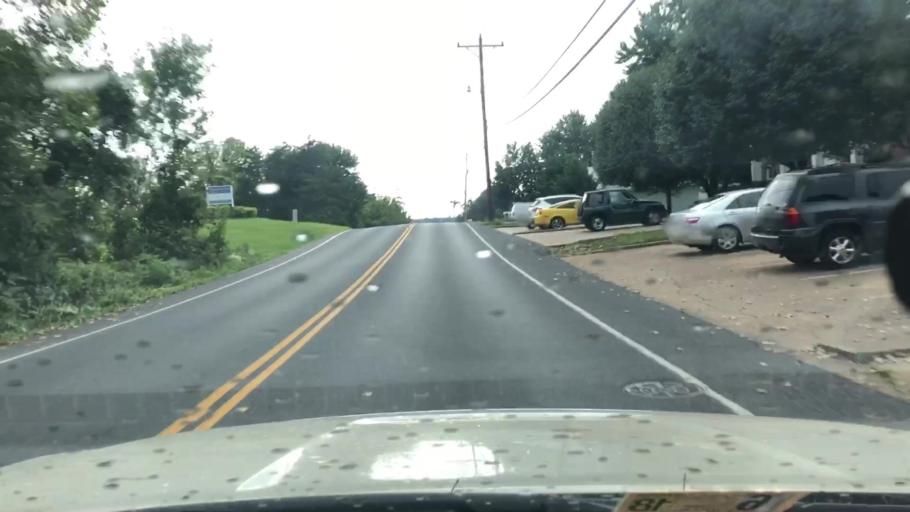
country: US
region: Virginia
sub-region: City of Harrisonburg
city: Harrisonburg
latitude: 38.4303
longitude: -78.8972
